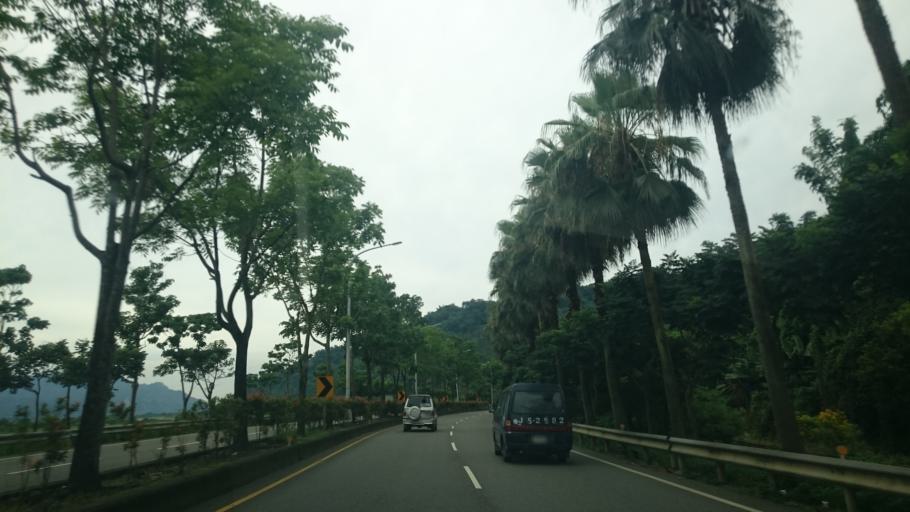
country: TW
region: Taiwan
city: Lugu
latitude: 23.8232
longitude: 120.8326
